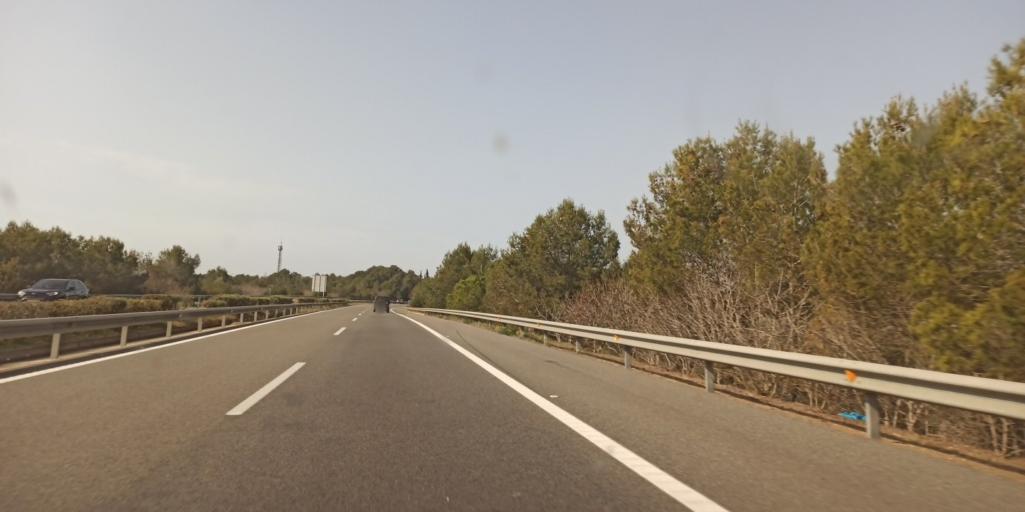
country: ES
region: Catalonia
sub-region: Provincia de Barcelona
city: Vilanova i la Geltru
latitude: 41.2465
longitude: 1.6924
